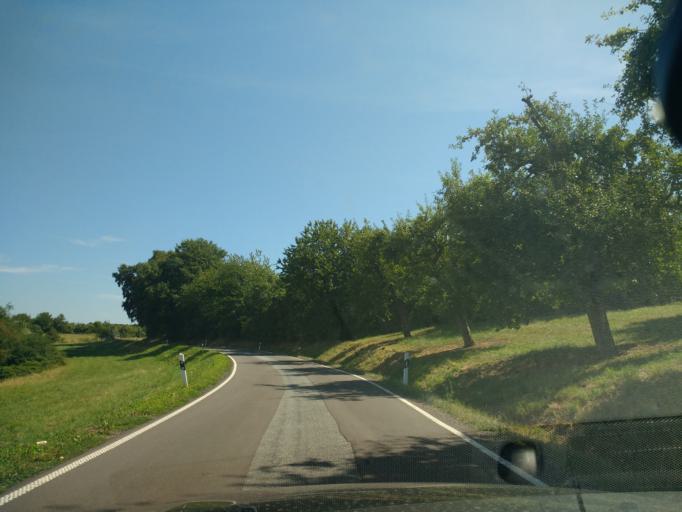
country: LU
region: Grevenmacher
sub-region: Canton de Remich
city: Remich
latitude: 49.5533
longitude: 6.3938
